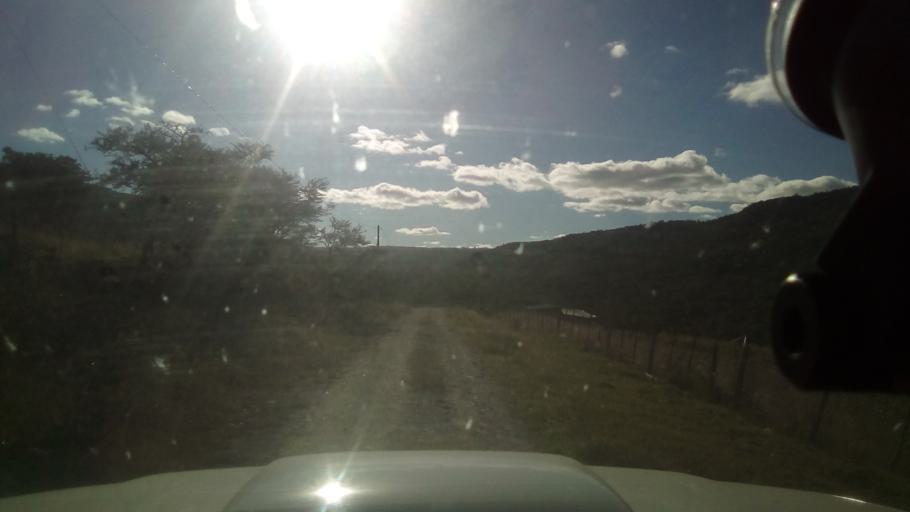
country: ZA
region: Eastern Cape
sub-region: Buffalo City Metropolitan Municipality
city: Bhisho
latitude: -32.7264
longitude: 27.3464
